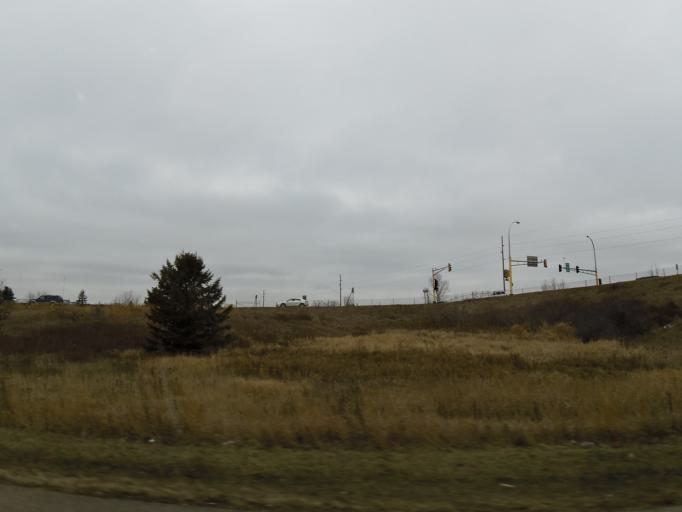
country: US
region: Minnesota
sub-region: Dakota County
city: Eagan
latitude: 44.7895
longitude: -93.2024
